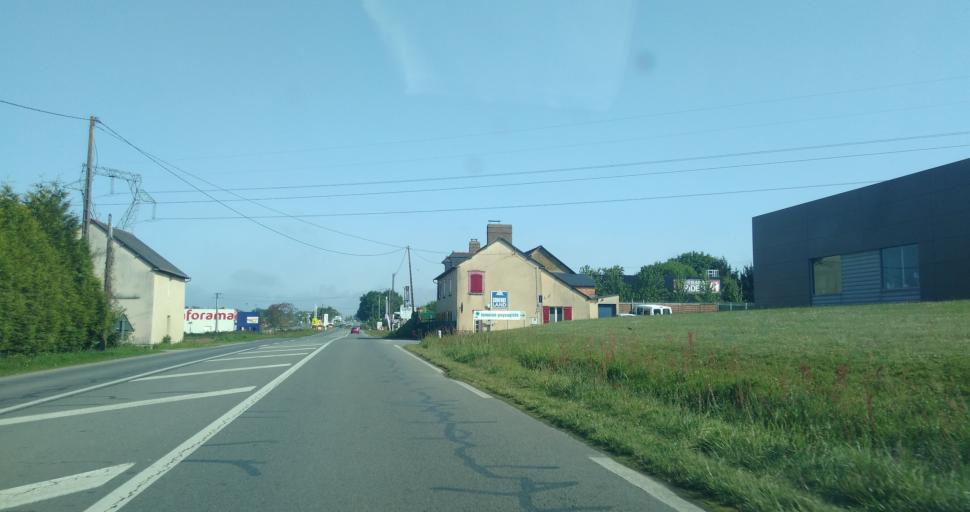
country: FR
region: Brittany
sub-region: Departement d'Ille-et-Vilaine
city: La Chapelle-des-Fougeretz
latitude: 48.1868
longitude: -1.7262
